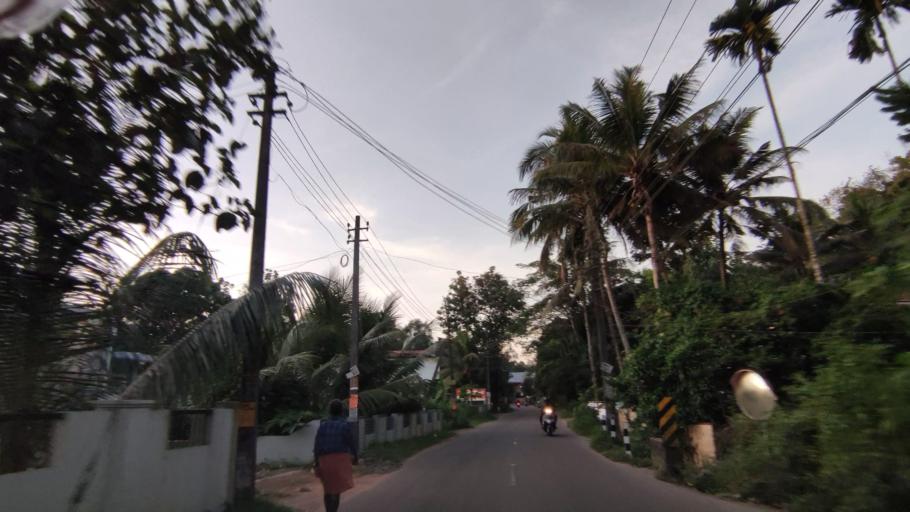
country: IN
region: Kerala
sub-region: Kottayam
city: Kottayam
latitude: 9.6510
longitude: 76.5091
